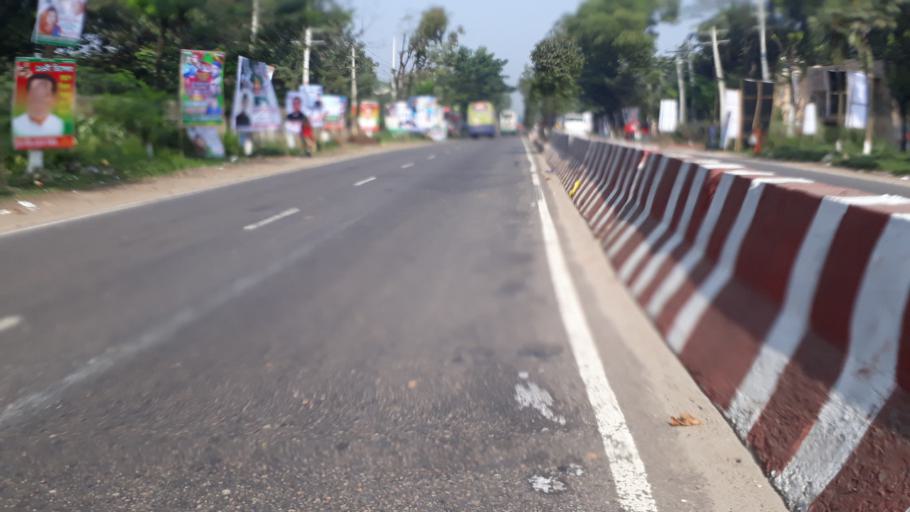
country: BD
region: Dhaka
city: Tungi
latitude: 23.8807
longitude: 90.2730
